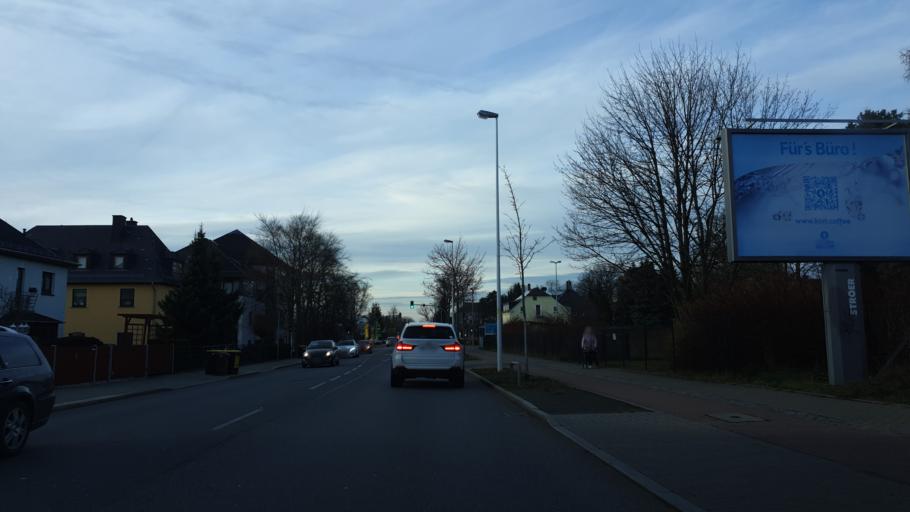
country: DE
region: Saxony
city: Chemnitz
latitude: 50.8149
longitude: 12.9537
